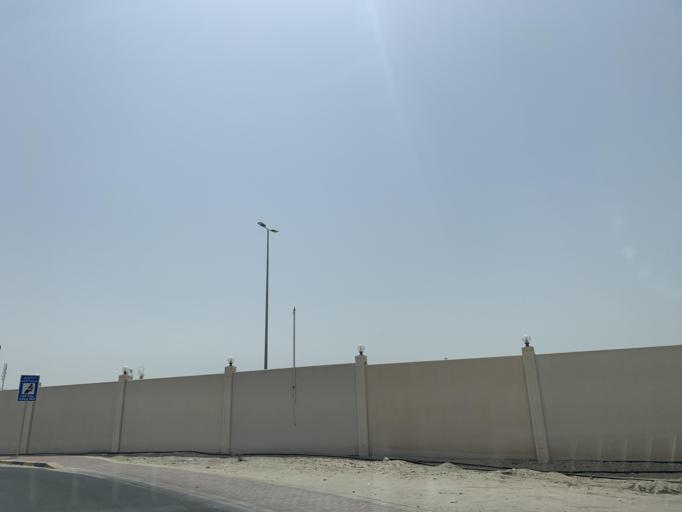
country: BH
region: Northern
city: Madinat `Isa
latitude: 26.1585
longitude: 50.5319
